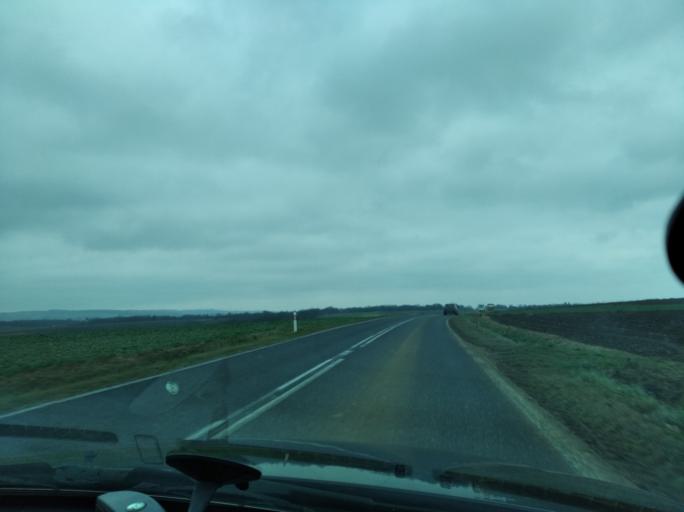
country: PL
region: Subcarpathian Voivodeship
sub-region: Powiat przeworski
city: Sietesz
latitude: 49.9936
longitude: 22.3765
